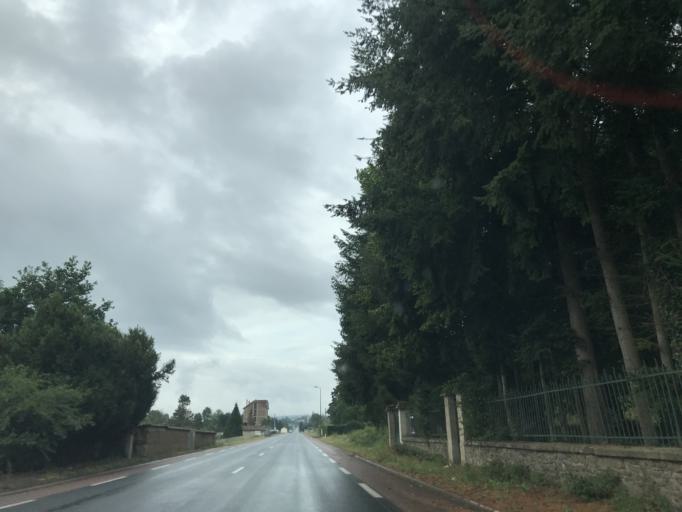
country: FR
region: Auvergne
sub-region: Departement du Puy-de-Dome
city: Arlanc
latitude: 45.4341
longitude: 3.7242
